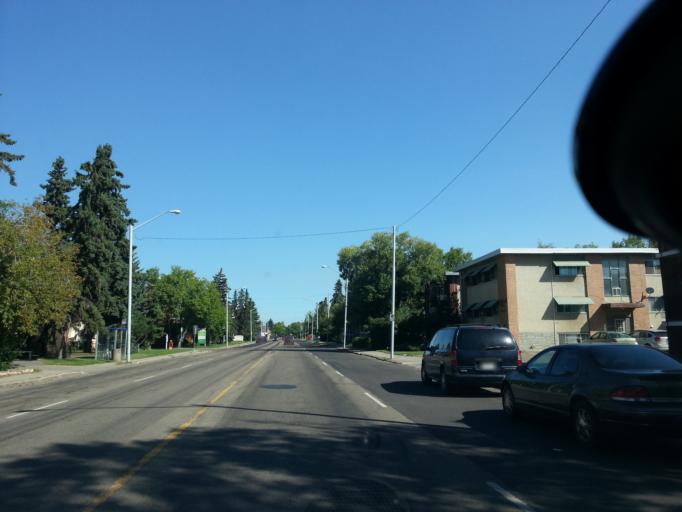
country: CA
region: Alberta
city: Edmonton
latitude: 53.5676
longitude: -113.5359
